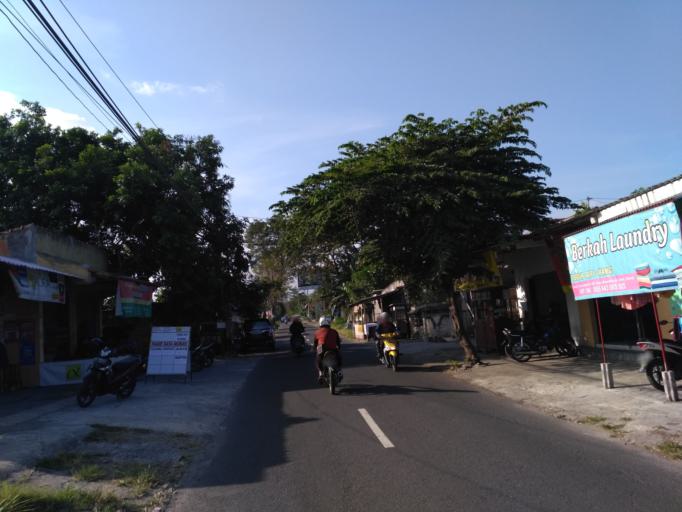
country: ID
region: Daerah Istimewa Yogyakarta
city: Depok
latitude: -7.7795
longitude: 110.4230
